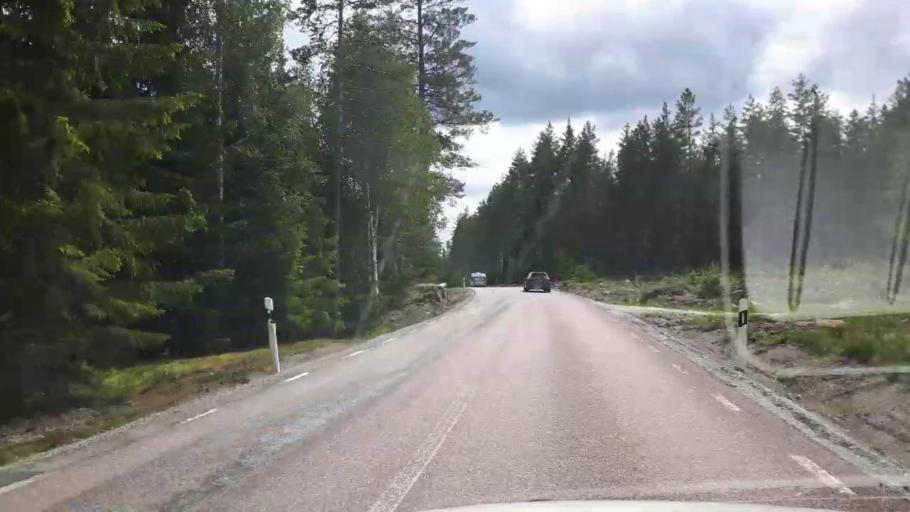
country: SE
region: Vaestmanland
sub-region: Skinnskattebergs Kommun
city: Skinnskatteberg
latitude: 59.8192
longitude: 15.8375
